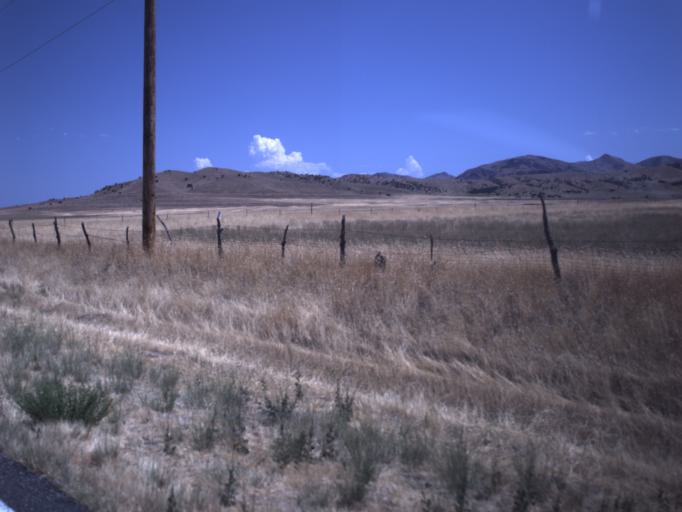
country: US
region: Utah
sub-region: Millard County
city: Delta
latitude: 39.4209
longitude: -112.3281
